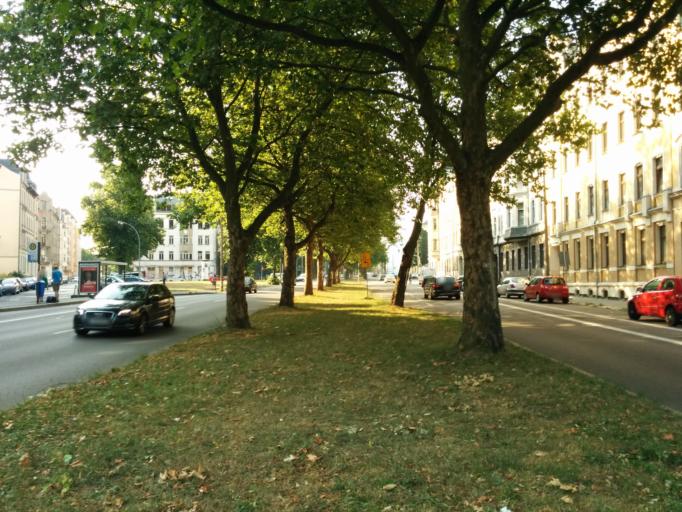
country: DE
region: Saxony
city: Chemnitz
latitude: 50.8217
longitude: 12.9267
